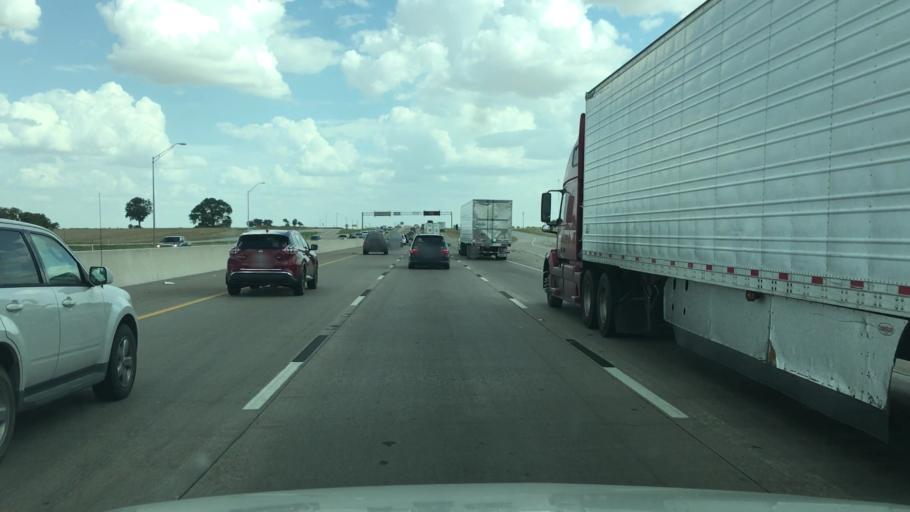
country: US
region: Texas
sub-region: Hill County
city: Hillsboro
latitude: 31.9527
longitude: -97.1136
